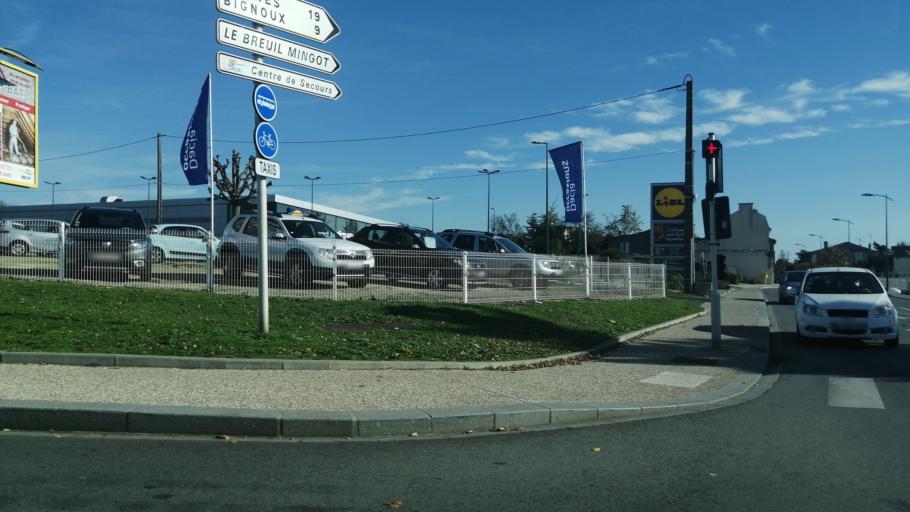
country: FR
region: Poitou-Charentes
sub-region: Departement de la Vienne
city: Poitiers
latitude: 46.5846
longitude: 0.3667
